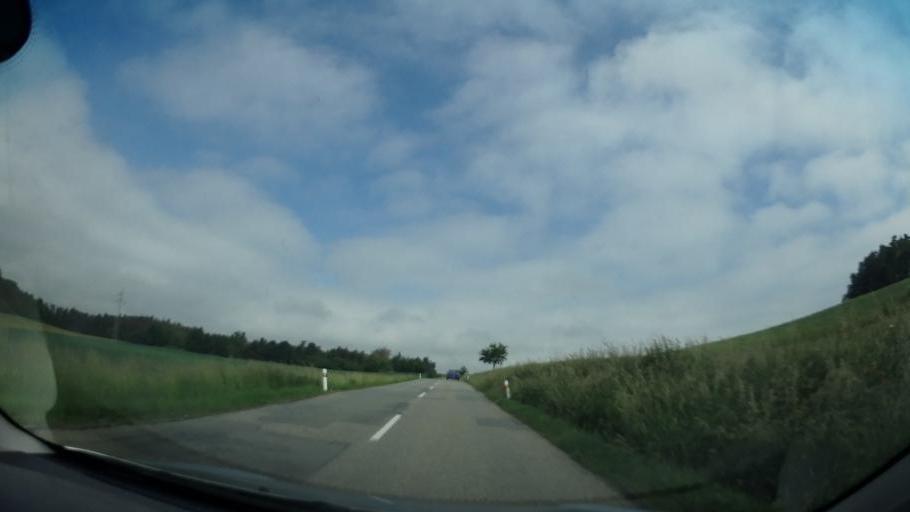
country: CZ
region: South Moravian
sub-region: Okres Brno-Venkov
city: Dolni Loucky
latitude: 49.3824
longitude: 16.3417
